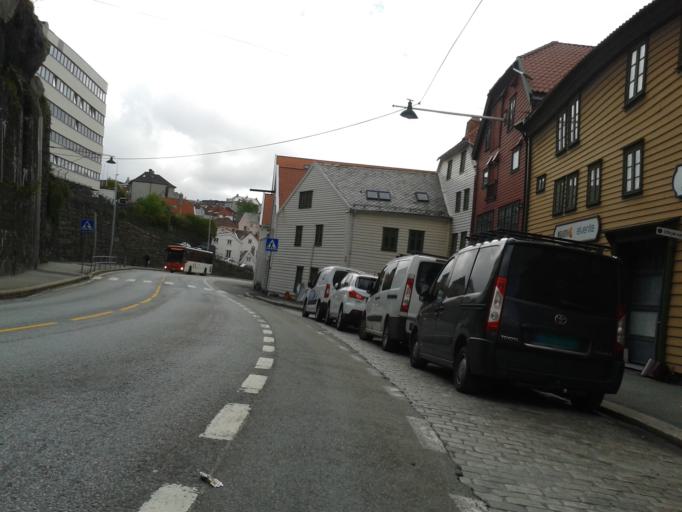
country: NO
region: Hordaland
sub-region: Bergen
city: Bergen
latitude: 60.4040
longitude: 5.3208
